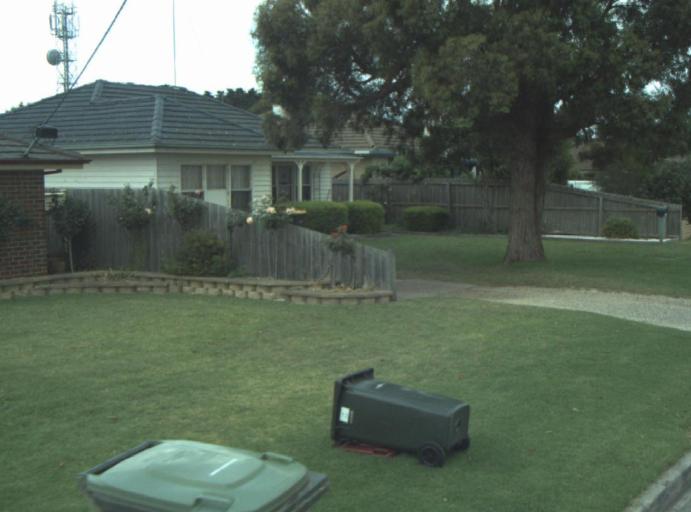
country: AU
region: Victoria
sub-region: Greater Geelong
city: East Geelong
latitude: -38.1713
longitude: 144.3990
